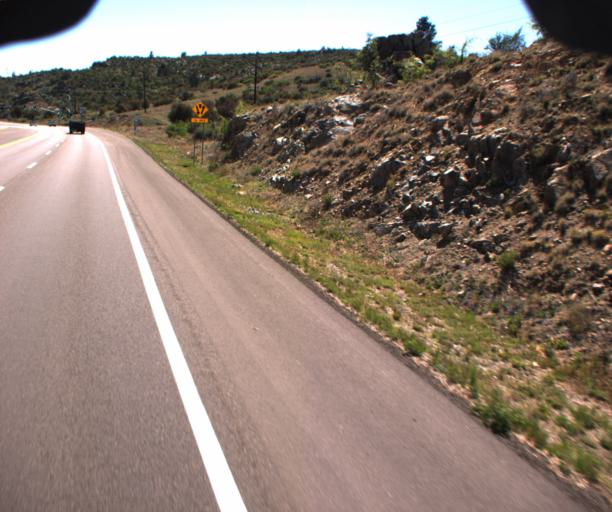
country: US
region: Arizona
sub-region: Yavapai County
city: Prescott
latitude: 34.5671
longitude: -112.4419
